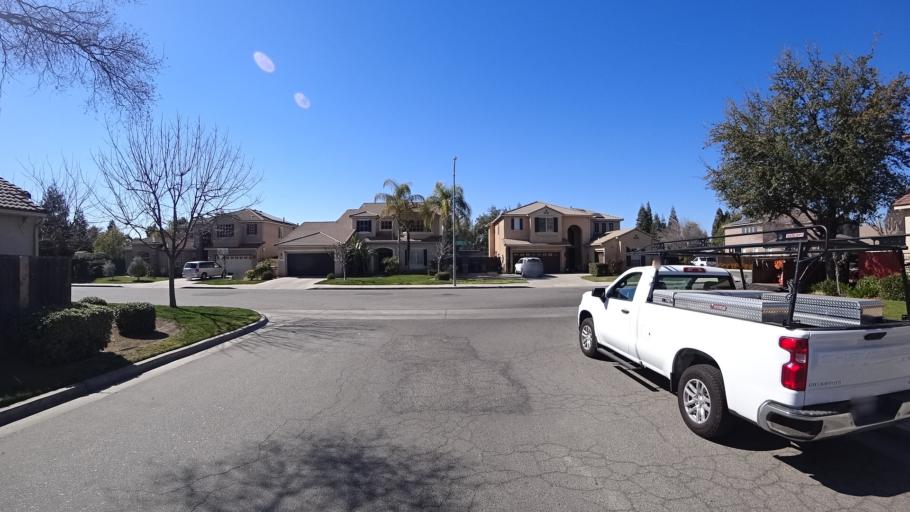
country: US
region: California
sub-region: Fresno County
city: Clovis
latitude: 36.8555
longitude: -119.7379
